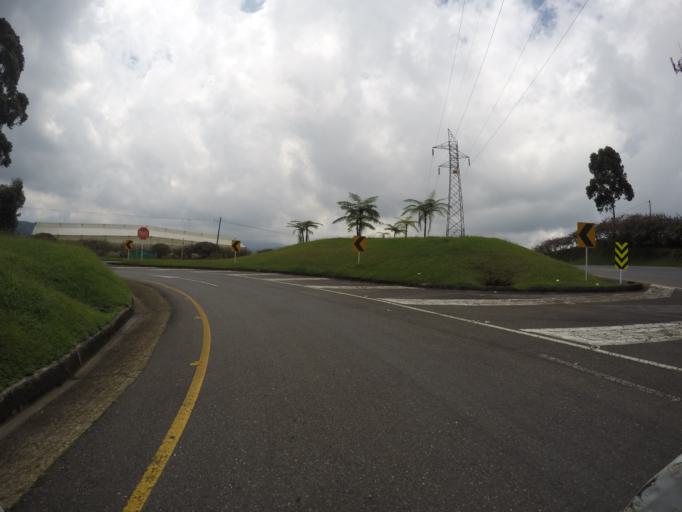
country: CO
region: Quindio
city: Filandia
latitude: 4.7103
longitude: -75.6140
